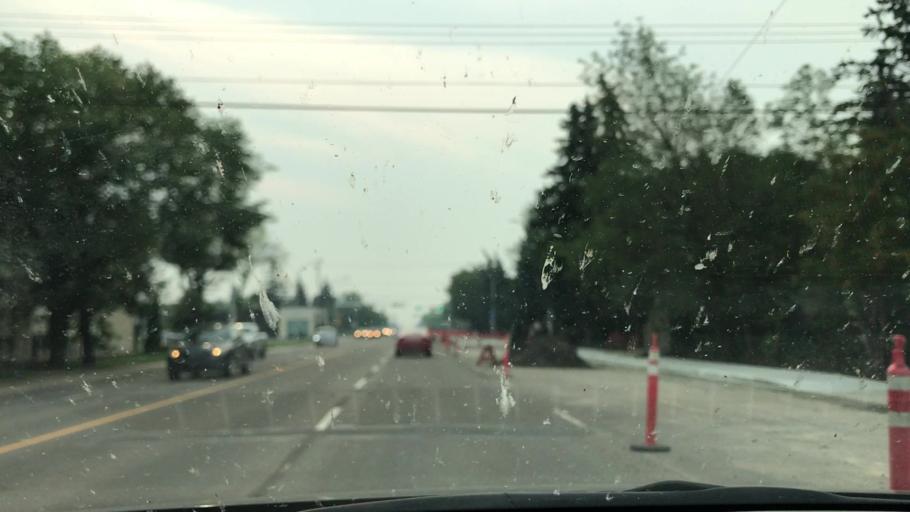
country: CA
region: Alberta
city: Edmonton
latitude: 53.5589
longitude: -113.5383
